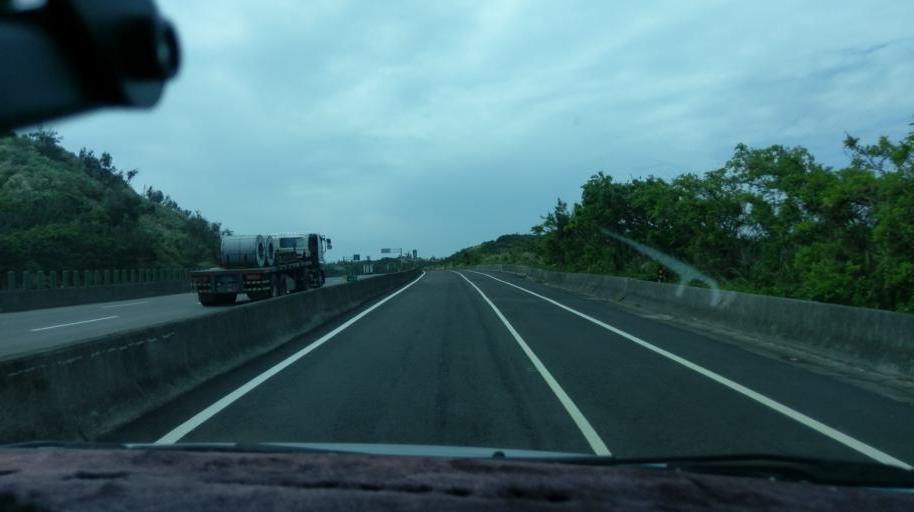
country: TW
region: Taiwan
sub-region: Miaoli
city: Miaoli
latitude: 24.5946
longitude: 120.7367
